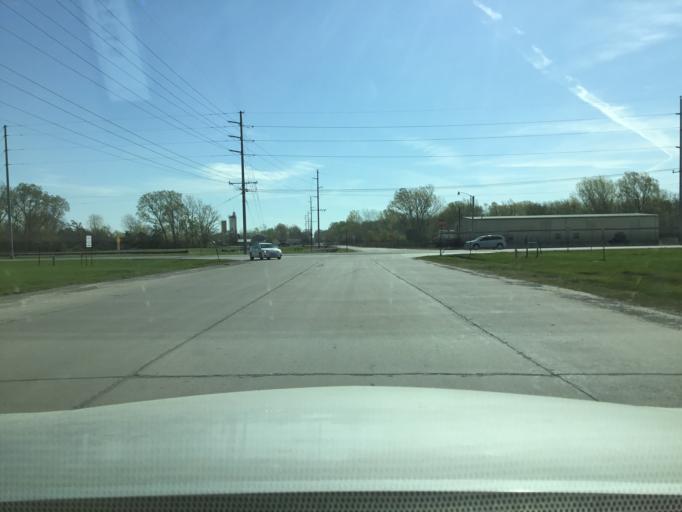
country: US
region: Kansas
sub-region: Neosho County
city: Chanute
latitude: 37.6963
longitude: -95.4535
